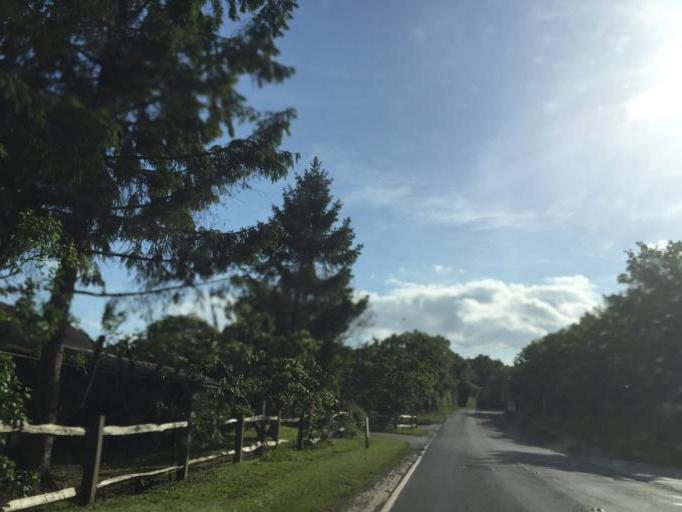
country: GB
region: England
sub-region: East Sussex
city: Crowborough
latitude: 51.0462
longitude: 0.1975
